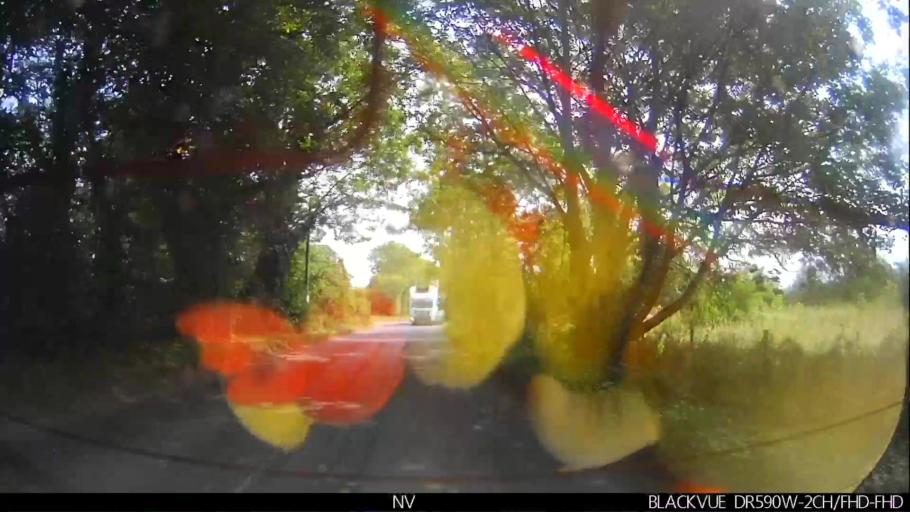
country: GB
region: England
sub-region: North Yorkshire
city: Great Habton
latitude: 54.2058
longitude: -0.8017
